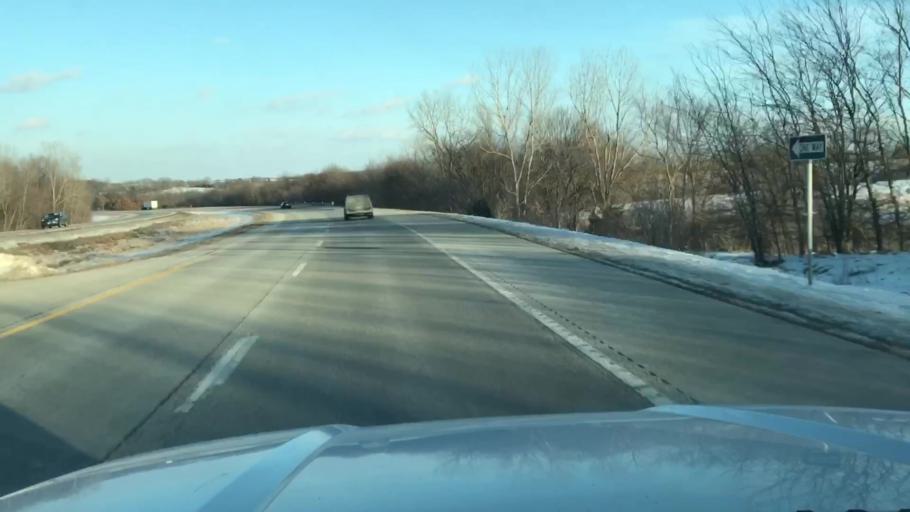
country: US
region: Missouri
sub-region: Clinton County
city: Gower
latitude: 39.7470
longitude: -94.6088
